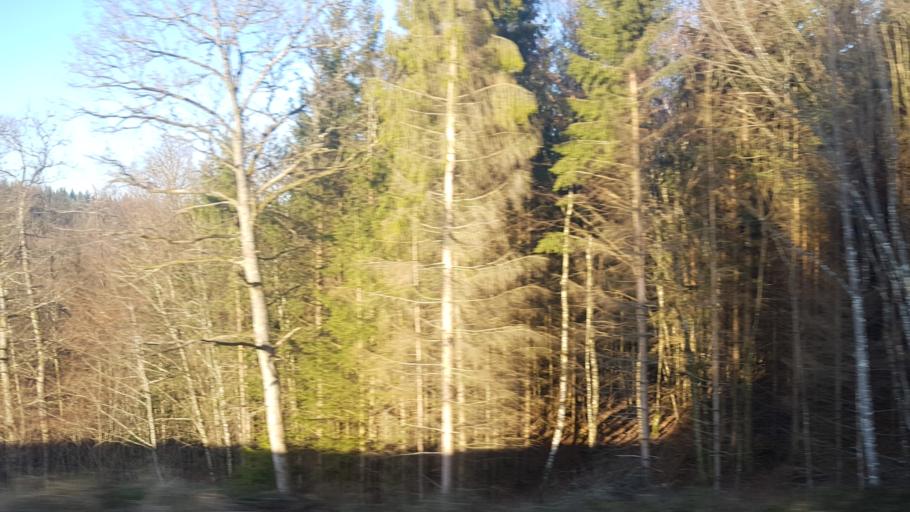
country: FR
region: Lorraine
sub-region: Departement des Vosges
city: Urimenil
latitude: 48.0802
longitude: 6.4238
